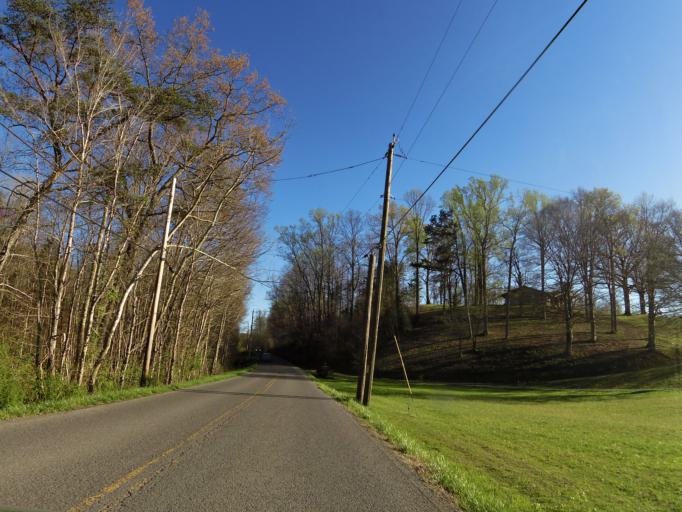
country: US
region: Tennessee
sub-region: Knox County
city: Mascot
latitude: 36.0019
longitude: -83.7663
